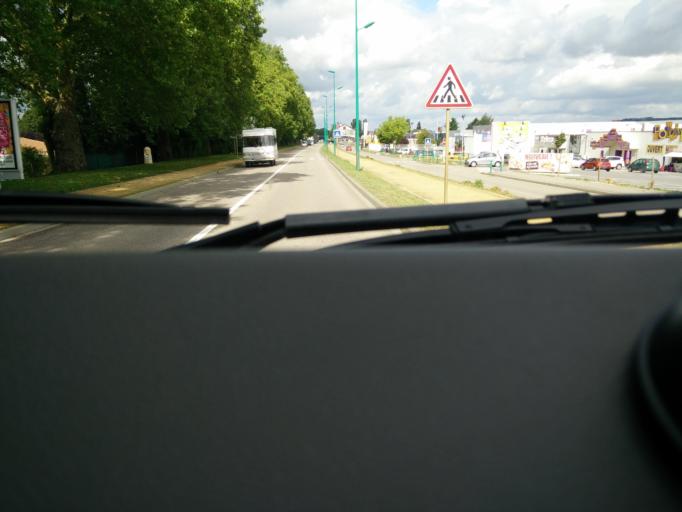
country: FR
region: Lorraine
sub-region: Departement de la Meuse
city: Verdun
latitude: 49.1462
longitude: 5.4061
